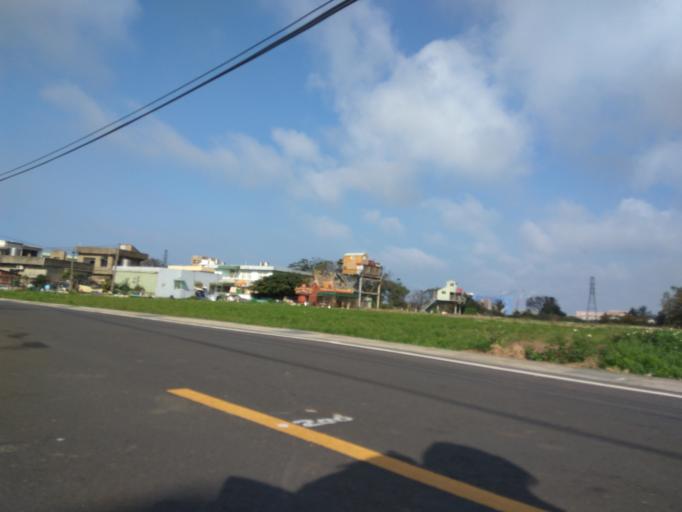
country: TW
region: Taiwan
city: Taoyuan City
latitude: 25.0631
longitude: 121.1731
